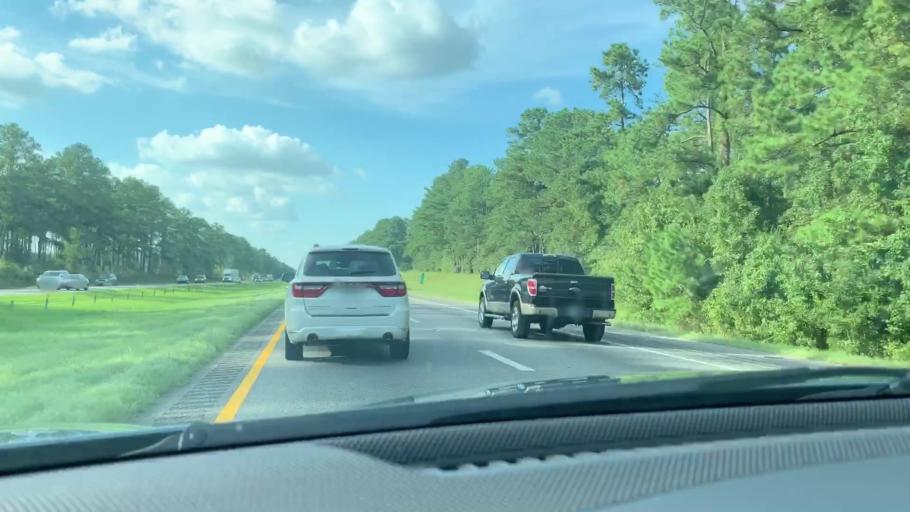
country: US
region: South Carolina
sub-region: Orangeburg County
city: Brookdale
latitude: 33.5386
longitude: -80.8073
